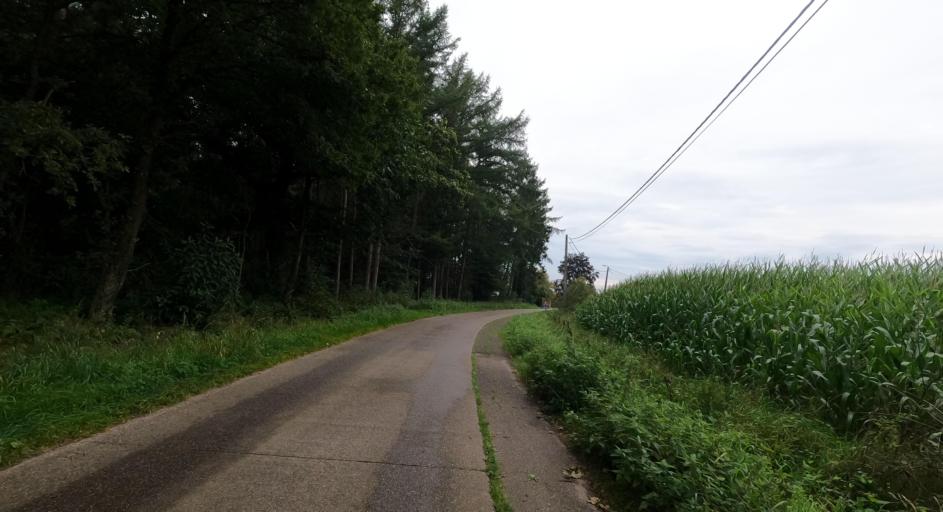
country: BE
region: Flanders
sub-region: Provincie Antwerpen
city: Lille
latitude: 51.2176
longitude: 4.8720
